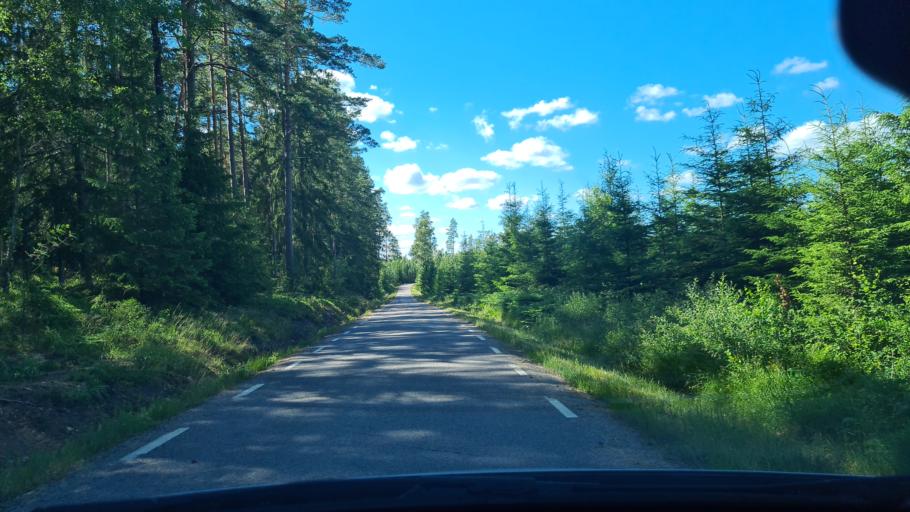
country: SE
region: OEstergoetland
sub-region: Norrkopings Kommun
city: Krokek
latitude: 58.7042
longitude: 16.4305
